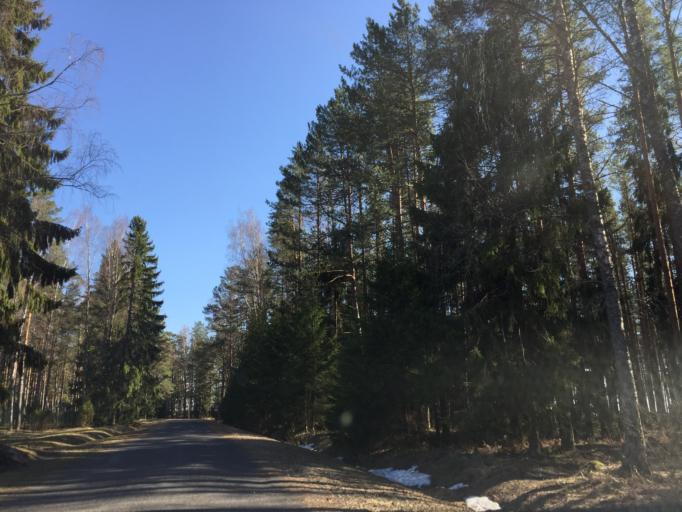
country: EE
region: Ida-Virumaa
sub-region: Johvi vald
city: Johvi
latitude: 59.0106
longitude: 27.4974
